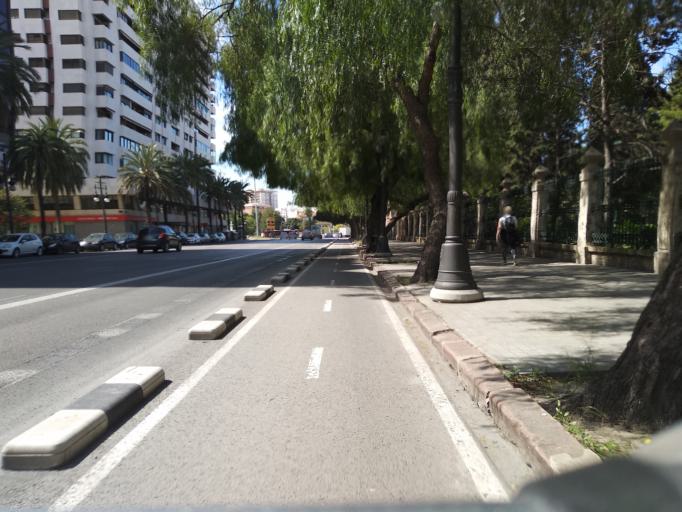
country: ES
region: Valencia
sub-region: Provincia de Valencia
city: Valencia
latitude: 39.4788
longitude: -0.3668
